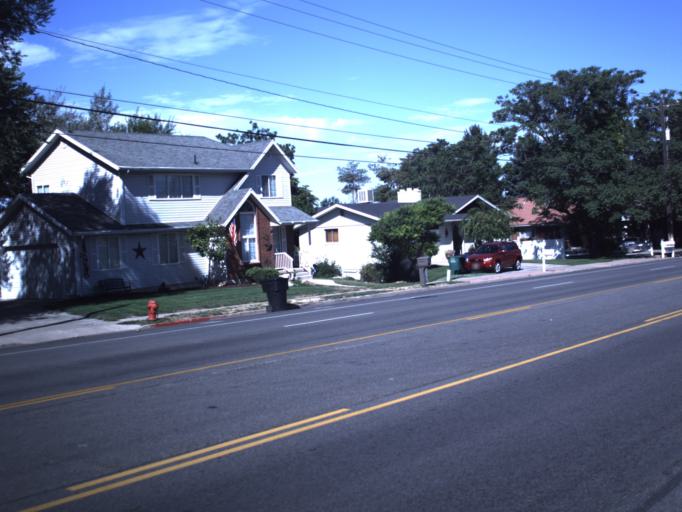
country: US
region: Utah
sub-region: Davis County
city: Kaysville
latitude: 41.0281
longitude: -111.9323
